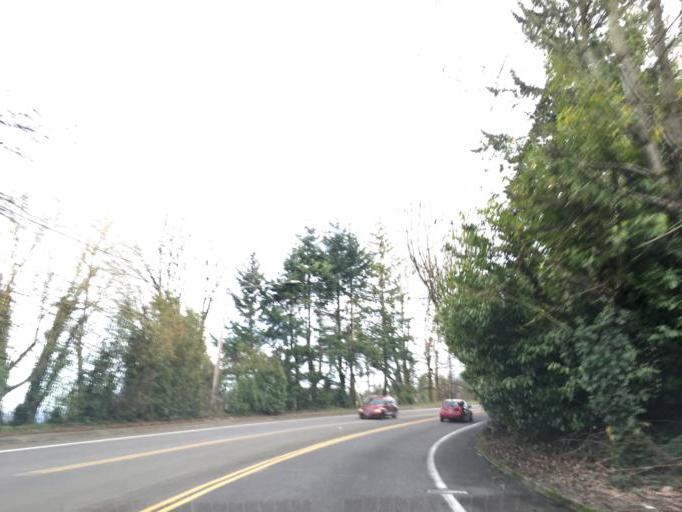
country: US
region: Oregon
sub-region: Clackamas County
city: Lake Oswego
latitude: 45.4671
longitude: -122.6841
